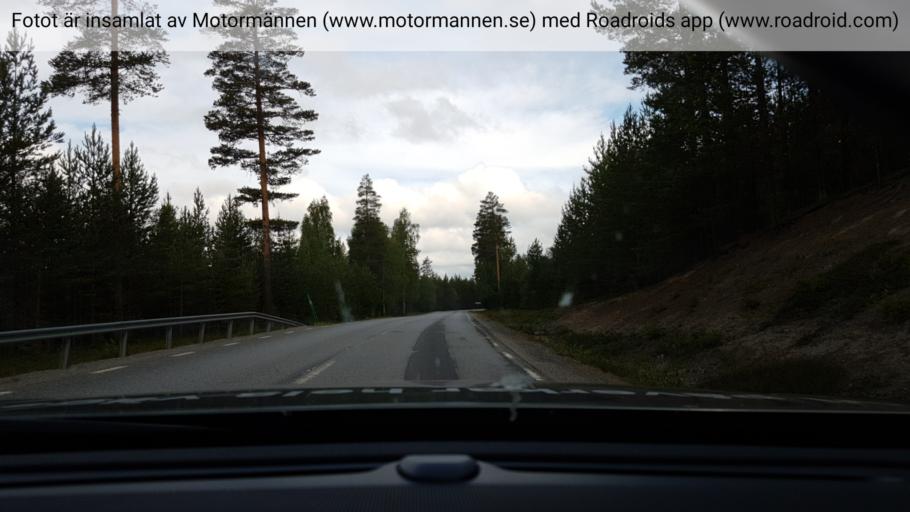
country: SE
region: Vaesterbotten
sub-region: Vindelns Kommun
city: Vindeln
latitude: 64.2472
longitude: 19.6489
